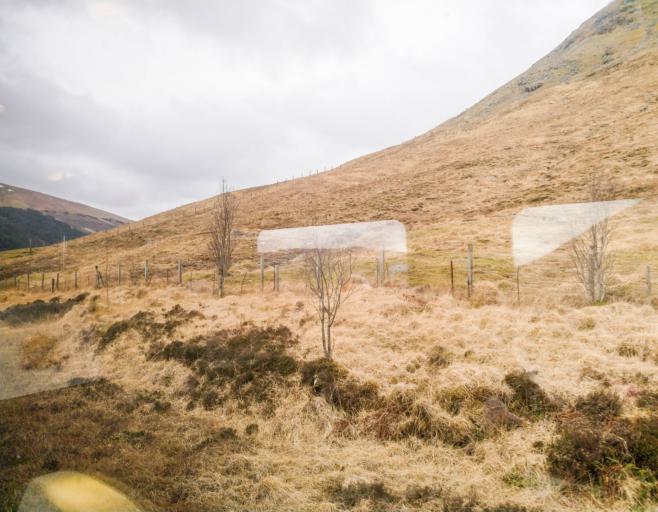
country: GB
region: Scotland
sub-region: Argyll and Bute
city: Garelochhead
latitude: 56.4878
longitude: -4.7139
